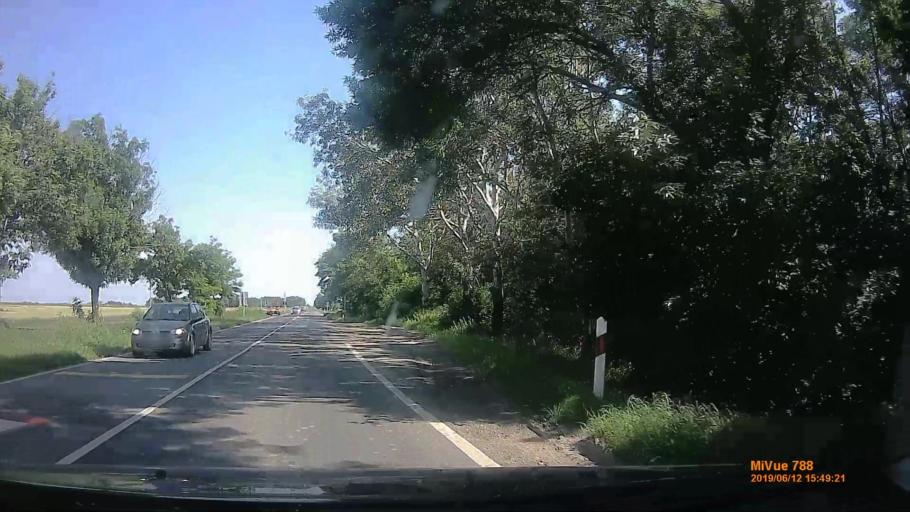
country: HU
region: Csongrad
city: Apatfalva
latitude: 46.1965
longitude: 20.5564
